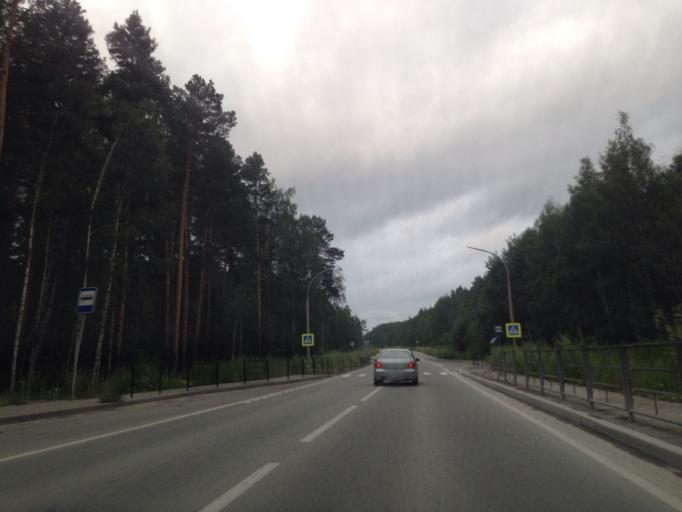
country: RU
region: Sverdlovsk
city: Istok
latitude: 56.8397
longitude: 60.7614
